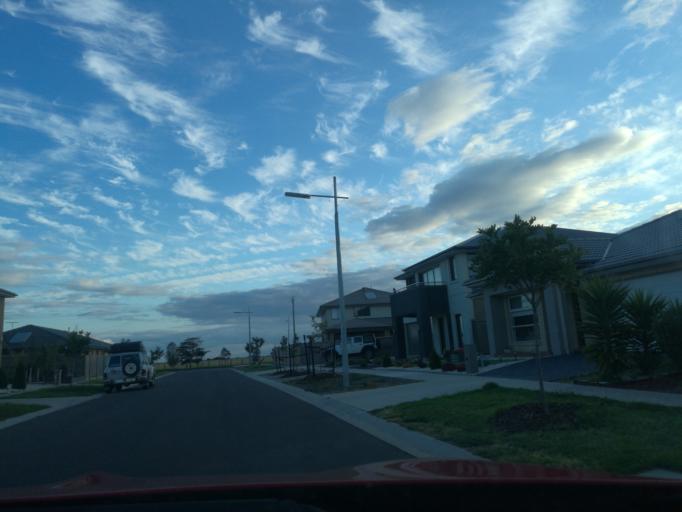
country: AU
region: Victoria
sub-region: Wyndham
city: Point Cook
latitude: -37.9170
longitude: 144.7835
